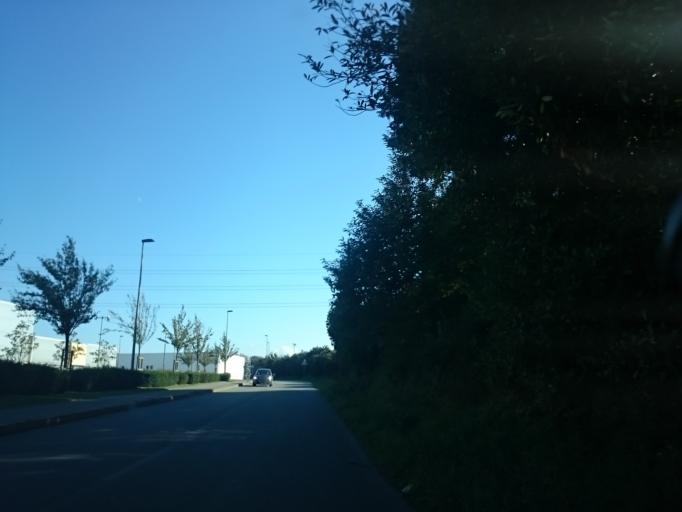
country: FR
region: Brittany
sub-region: Departement du Finistere
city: Gouesnou
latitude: 48.4269
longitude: -4.4735
